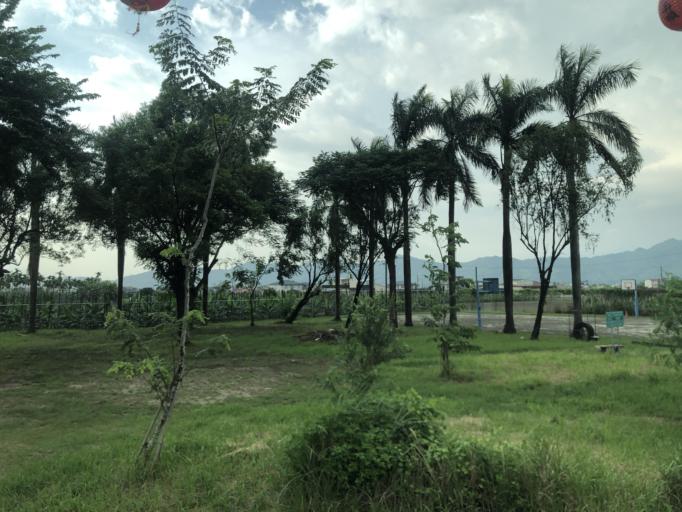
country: TW
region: Taiwan
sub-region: Pingtung
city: Pingtung
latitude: 22.8660
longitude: 120.5424
